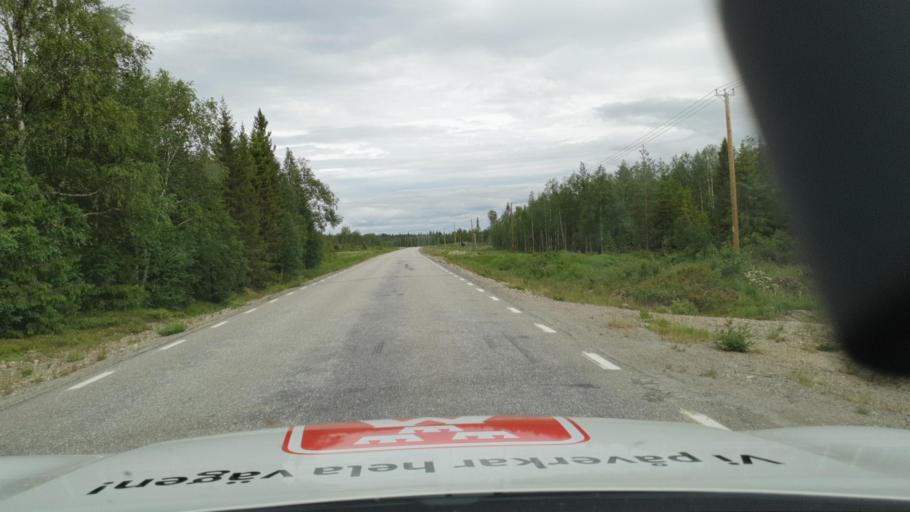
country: SE
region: Vaesterbotten
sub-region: Lycksele Kommun
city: Soderfors
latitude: 64.3701
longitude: 18.0700
